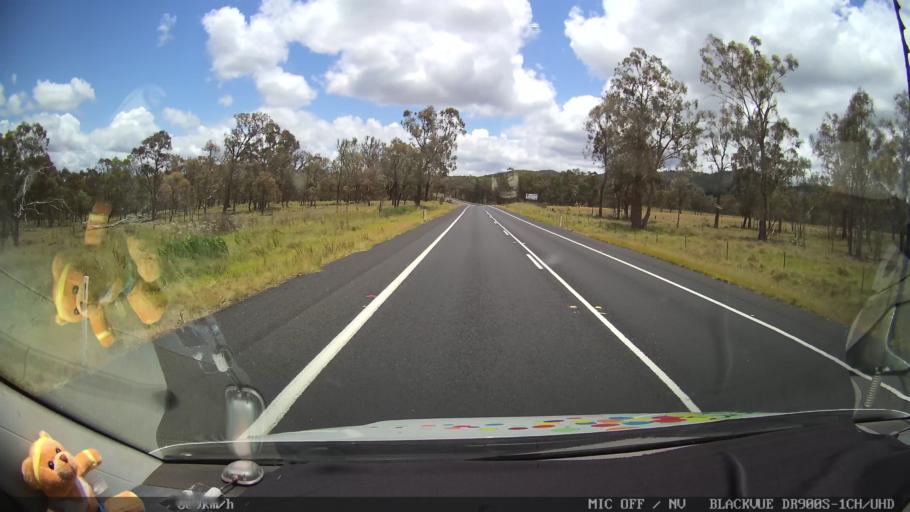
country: AU
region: New South Wales
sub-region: Glen Innes Severn
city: Glen Innes
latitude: -29.3629
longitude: 151.8988
